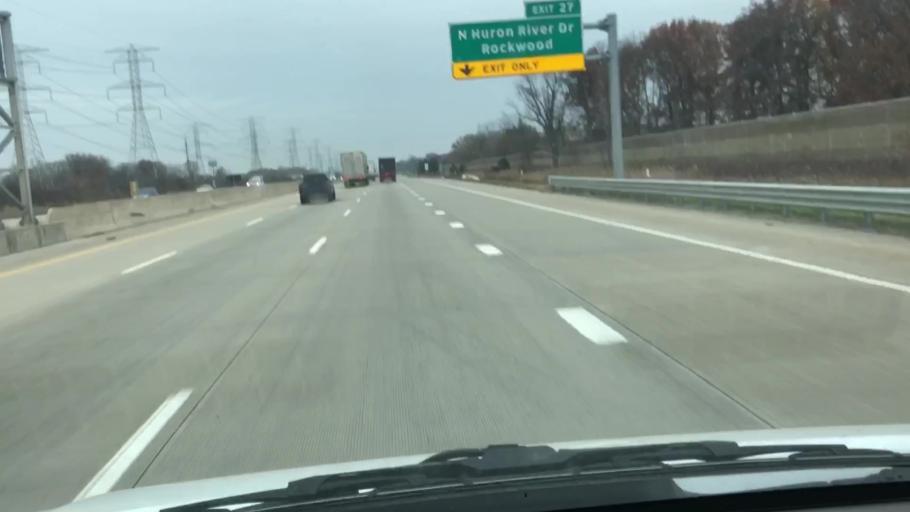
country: US
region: Michigan
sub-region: Wayne County
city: Rockwood
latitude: 42.0794
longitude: -83.2451
